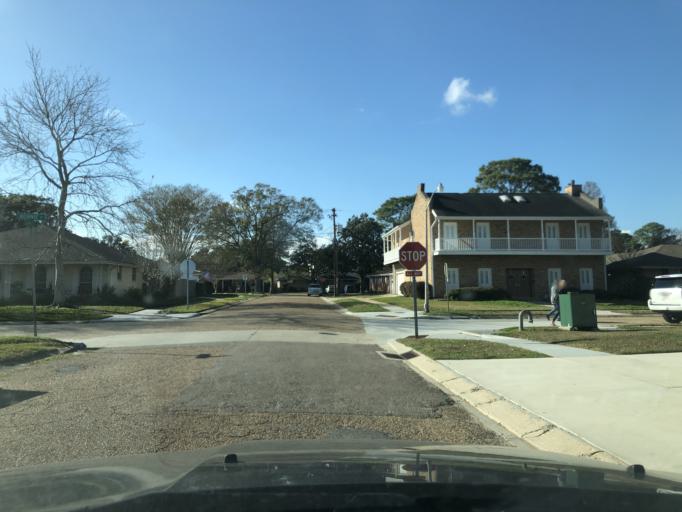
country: US
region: Louisiana
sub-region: Jefferson Parish
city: Metairie Terrace
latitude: 29.9903
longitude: -90.1660
